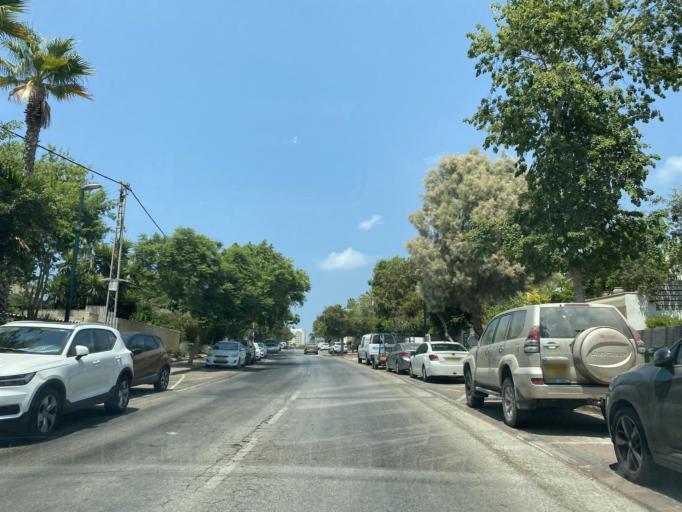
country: IL
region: Tel Aviv
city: Herzliya Pituah
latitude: 32.1708
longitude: 34.8040
